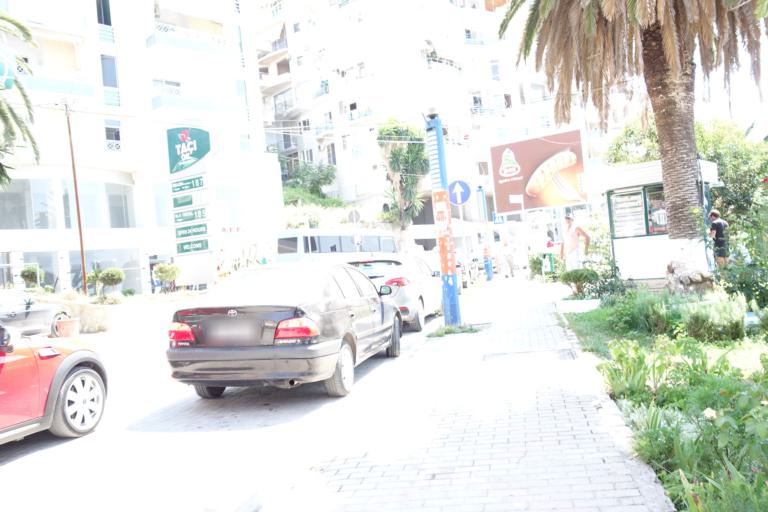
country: AL
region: Vlore
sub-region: Rrethi i Sarandes
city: Sarande
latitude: 39.8736
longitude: 20.0115
